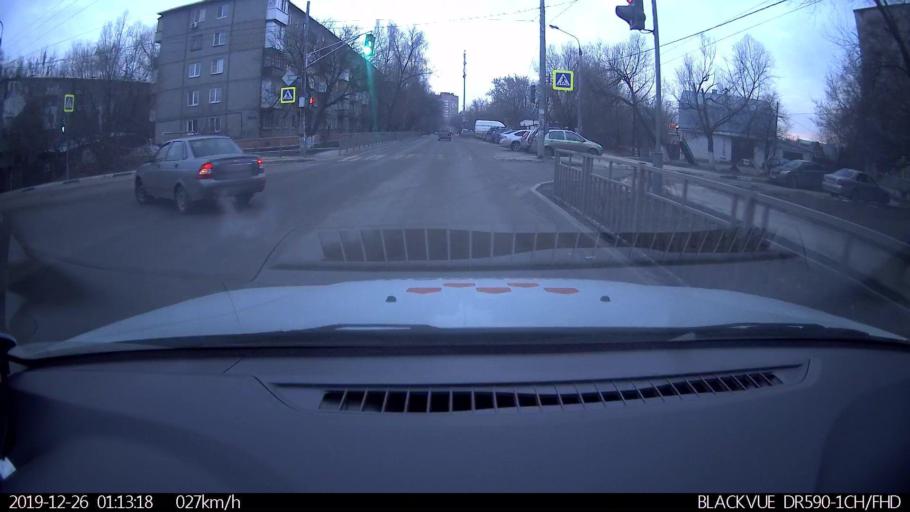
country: RU
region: Nizjnij Novgorod
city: Nizhniy Novgorod
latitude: 56.2789
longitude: 43.9115
